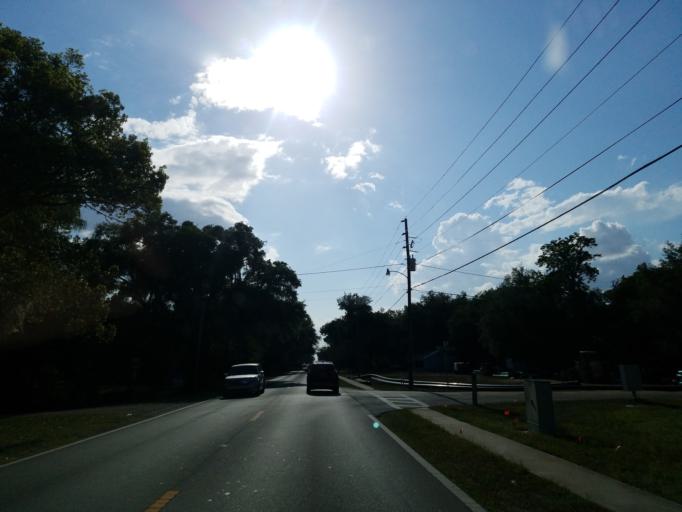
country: US
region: Florida
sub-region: Lake County
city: Fruitland Park
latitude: 28.8616
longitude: -81.9149
